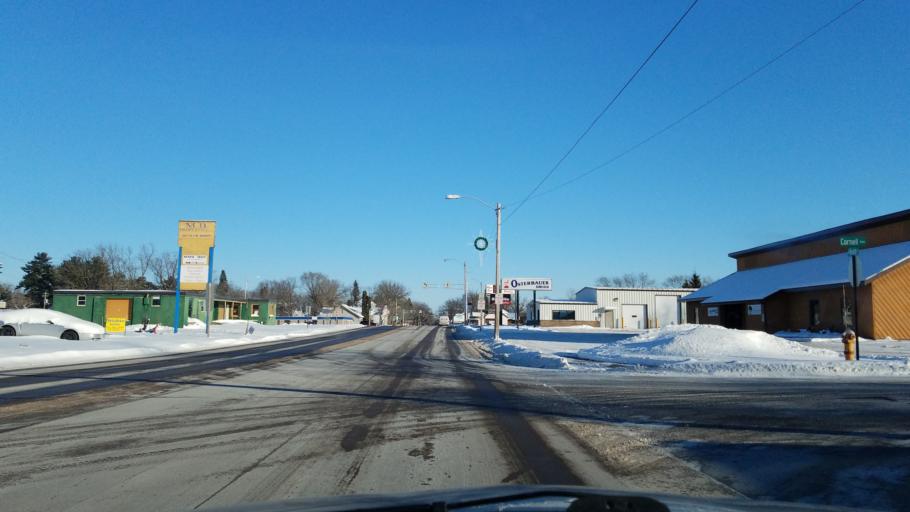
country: US
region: Wisconsin
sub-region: Barron County
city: Rice Lake
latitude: 45.5087
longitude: -91.7416
